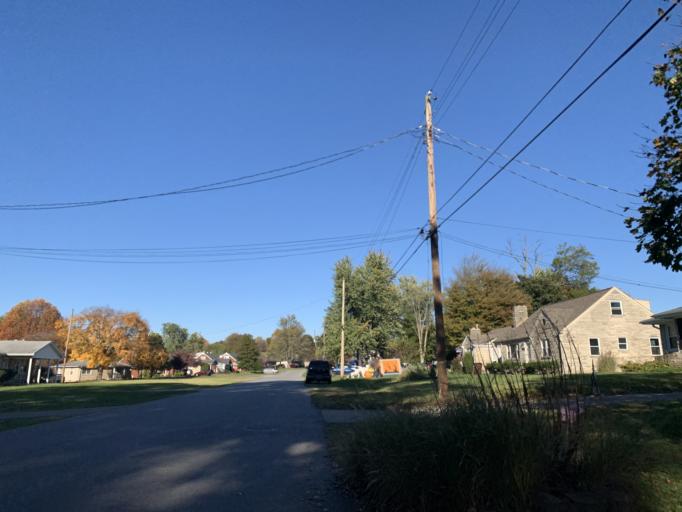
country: US
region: Kentucky
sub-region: Jefferson County
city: Saint Dennis
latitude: 38.1699
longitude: -85.8297
